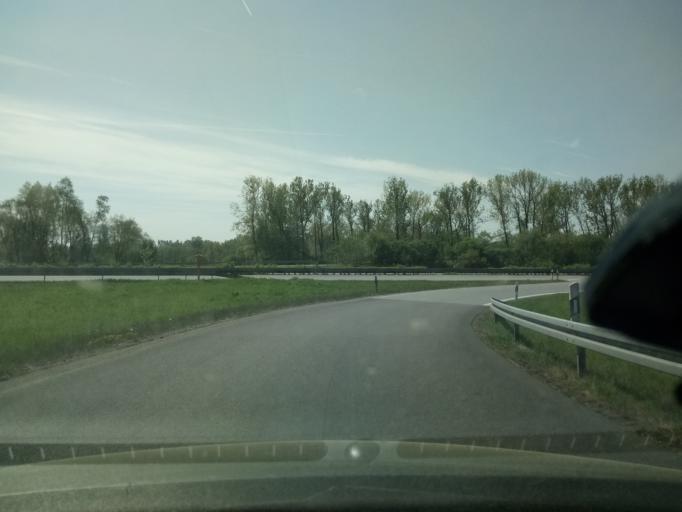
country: DE
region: Bavaria
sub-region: Upper Bavaria
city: Winhoring
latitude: 48.2528
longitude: 12.6663
